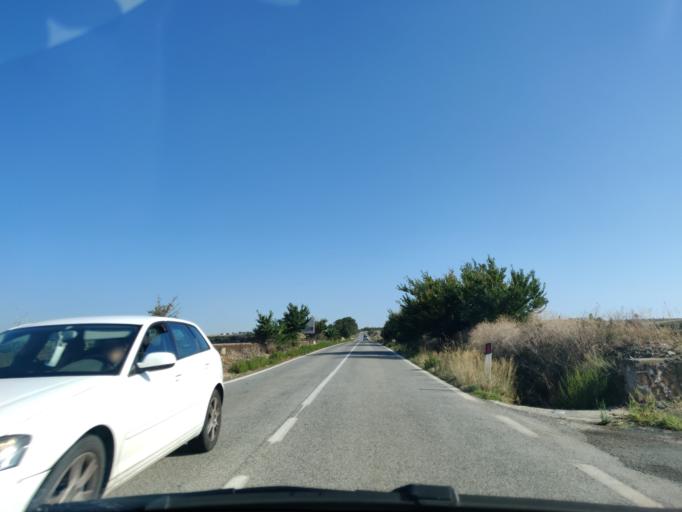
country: IT
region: Latium
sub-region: Provincia di Viterbo
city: Tarquinia
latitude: 42.2173
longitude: 11.7837
